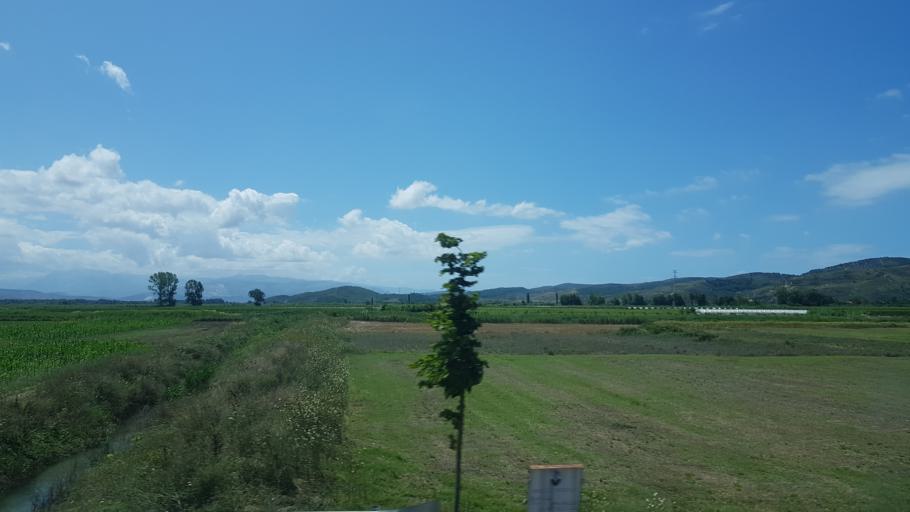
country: AL
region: Fier
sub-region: Rrethi i Fierit
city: Frakulla e Madhe
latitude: 40.6039
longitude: 19.5526
